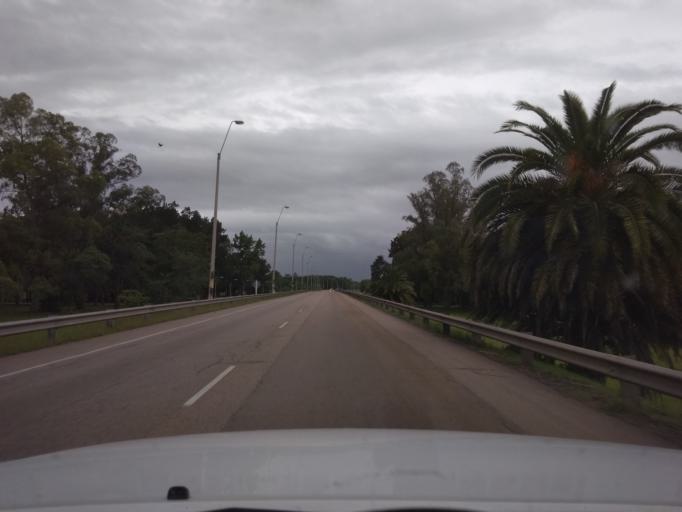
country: UY
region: Canelones
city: Canelones
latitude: -34.5258
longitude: -56.2711
